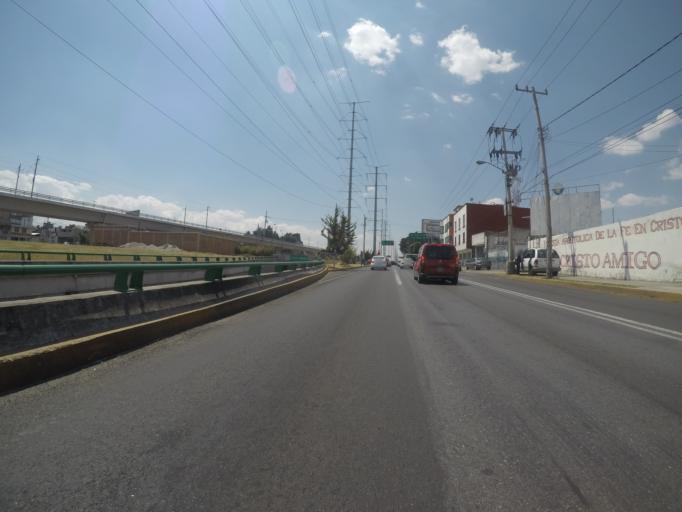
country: MX
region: Mexico
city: San Buenaventura
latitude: 19.2691
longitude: -99.6581
